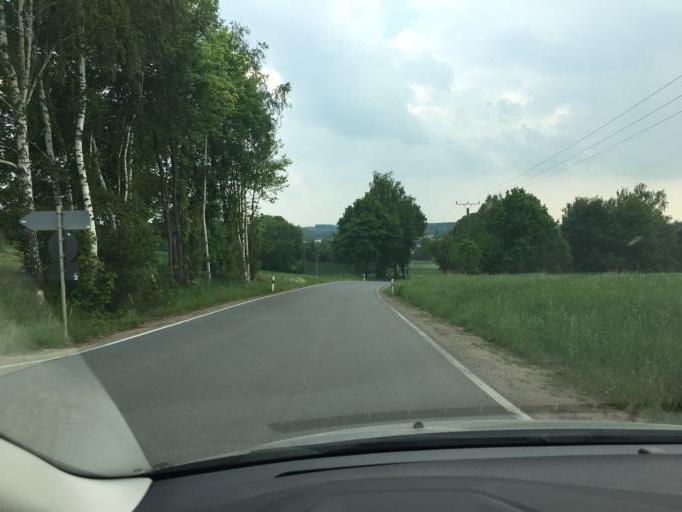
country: DE
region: Saxony
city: Rochlitz
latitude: 51.0595
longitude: 12.8050
